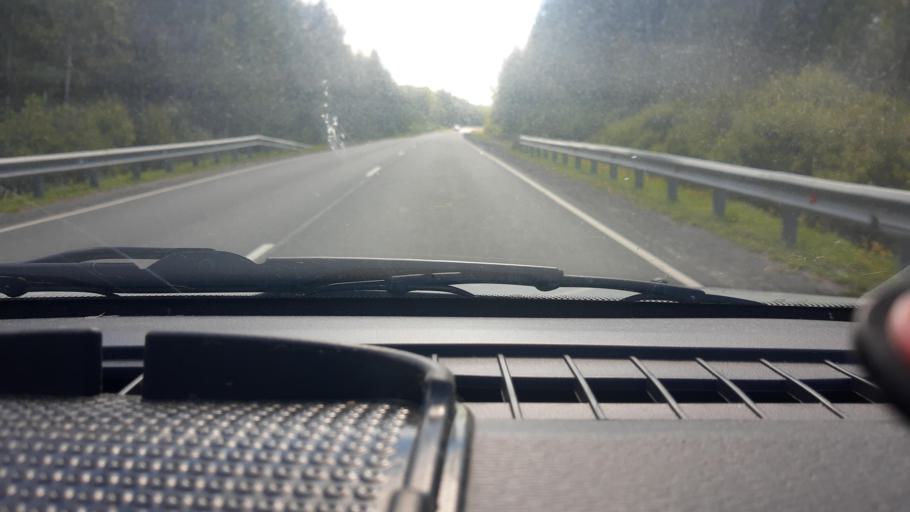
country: RU
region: Nizjnij Novgorod
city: Arzamas
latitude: 55.4210
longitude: 43.9103
